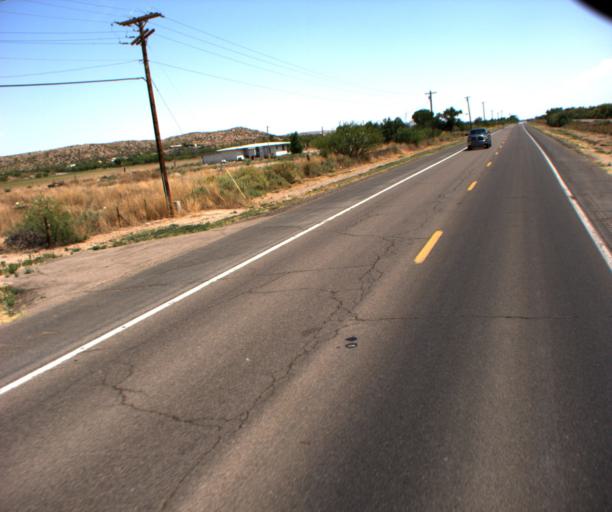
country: US
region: Arizona
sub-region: Greenlee County
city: Clifton
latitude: 32.7029
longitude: -109.0910
